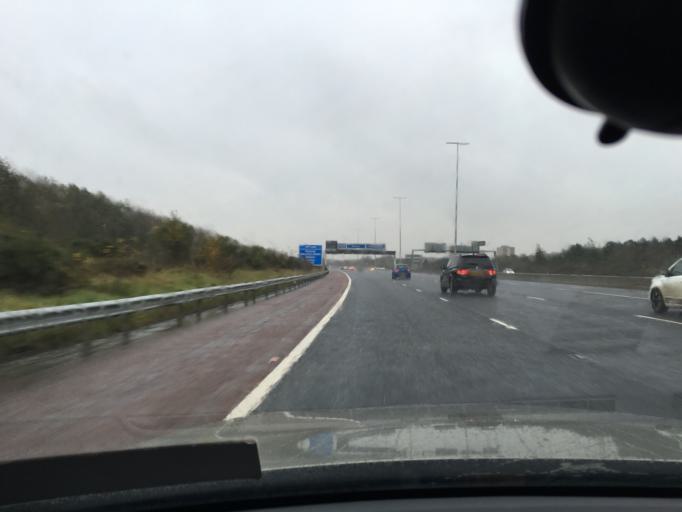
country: GB
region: Northern Ireland
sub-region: Newtownabbey District
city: Newtownabbey
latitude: 54.6396
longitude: -5.9182
